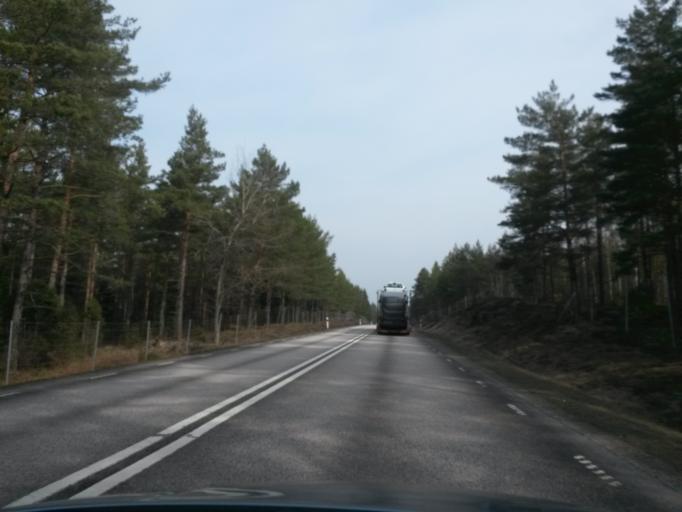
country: SE
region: Vaestra Goetaland
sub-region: Gullspangs Kommun
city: Hova
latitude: 58.8363
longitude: 14.1907
